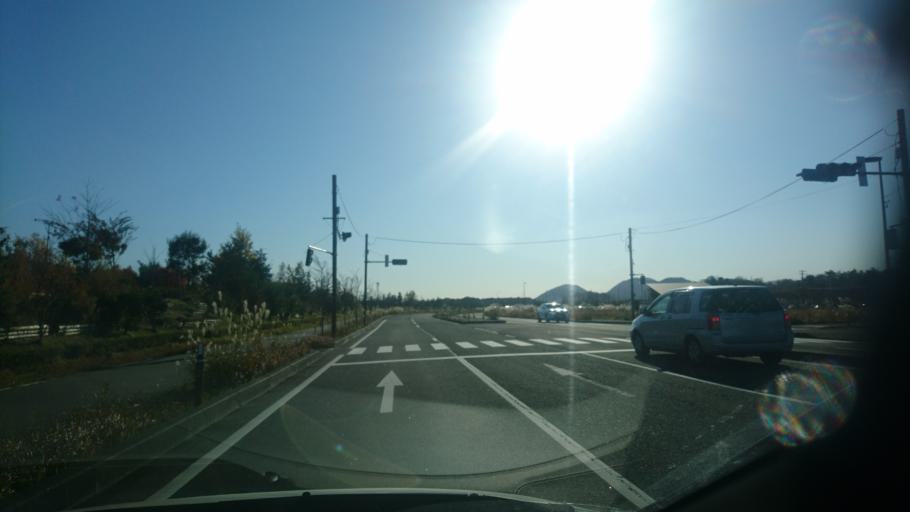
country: JP
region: Miyagi
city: Tomiya
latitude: 38.4706
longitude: 140.8916
